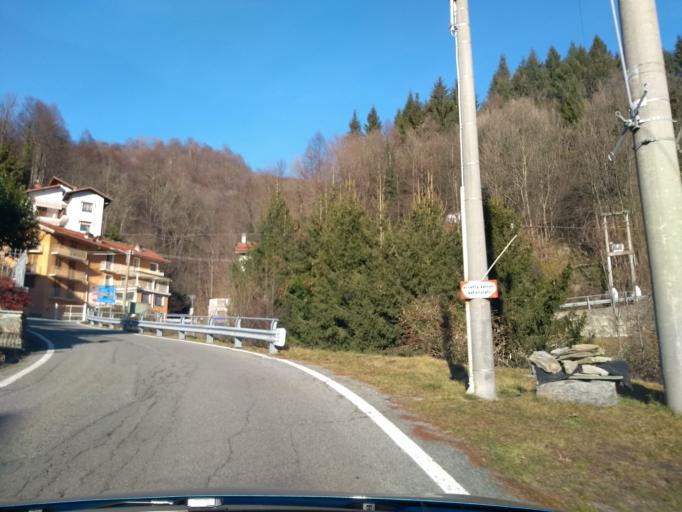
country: IT
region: Piedmont
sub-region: Provincia di Torino
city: Pessinetto
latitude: 45.2870
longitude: 7.4162
